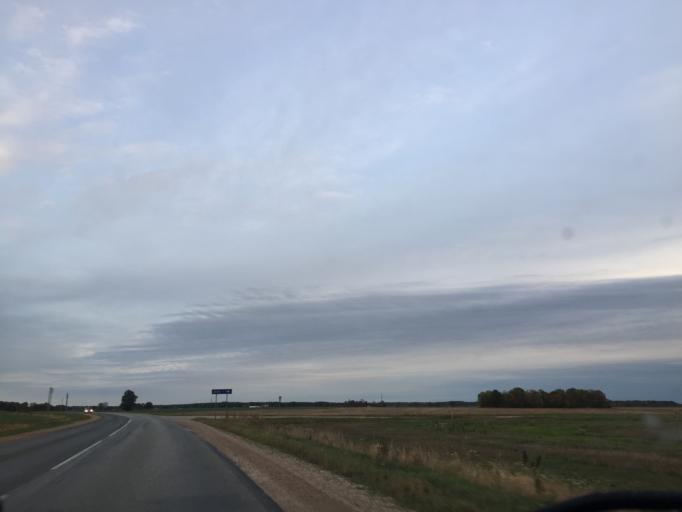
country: LV
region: Dobeles Rajons
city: Dobele
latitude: 56.6894
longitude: 23.3687
